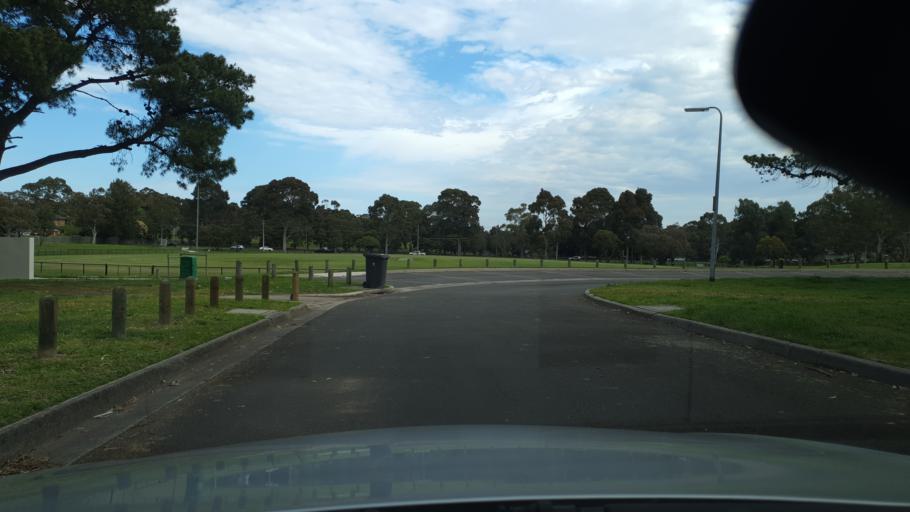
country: AU
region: Victoria
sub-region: Greater Dandenong
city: Noble Park North
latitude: -37.9335
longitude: 145.1774
